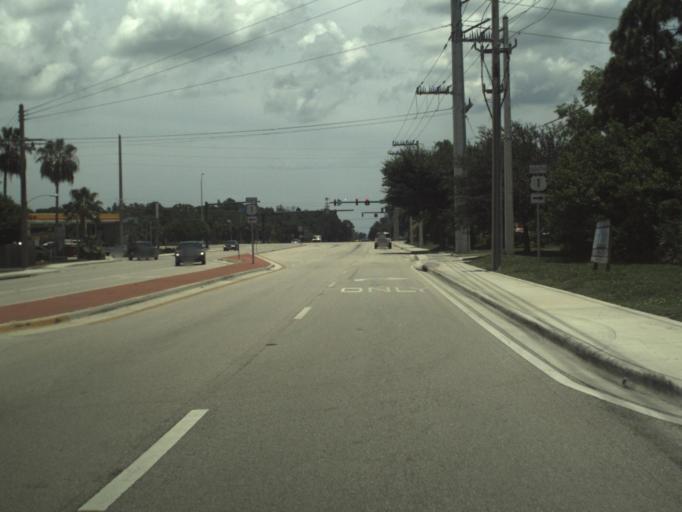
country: US
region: Florida
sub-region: Martin County
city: Port Salerno
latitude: 27.1332
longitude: -80.2085
